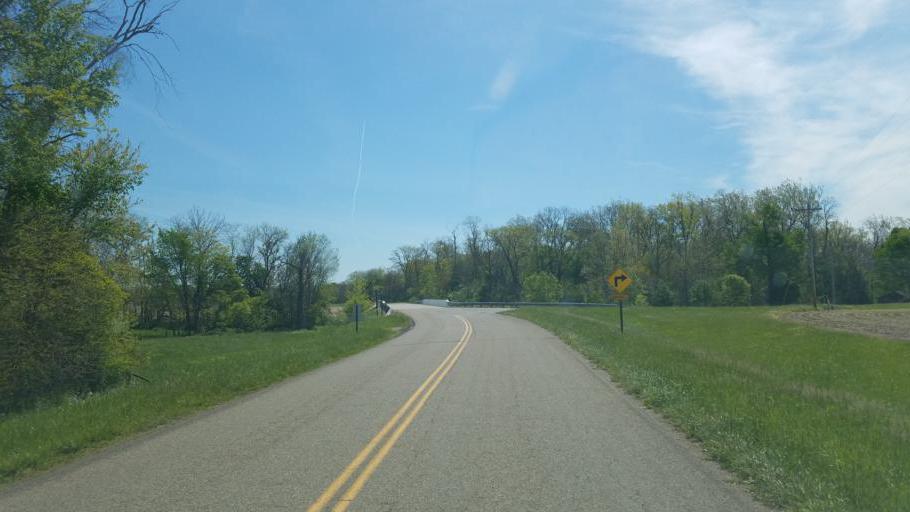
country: US
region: Ohio
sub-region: Knox County
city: Fredericktown
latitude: 40.4391
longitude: -82.5390
